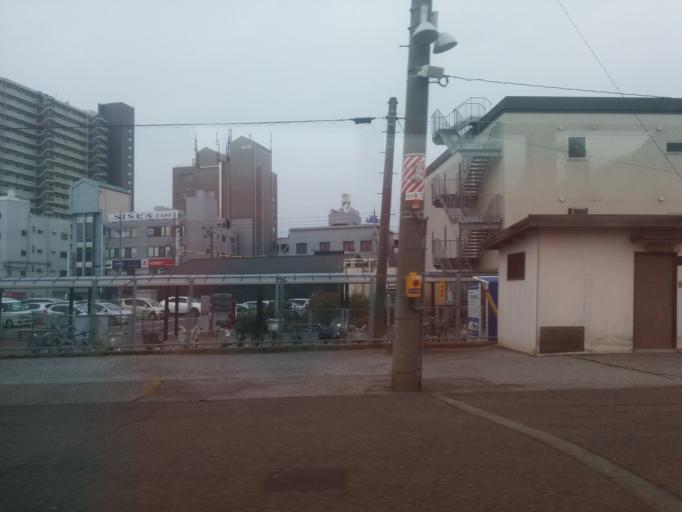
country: JP
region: Shiga Prefecture
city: Hikone
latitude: 35.2714
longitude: 136.2630
